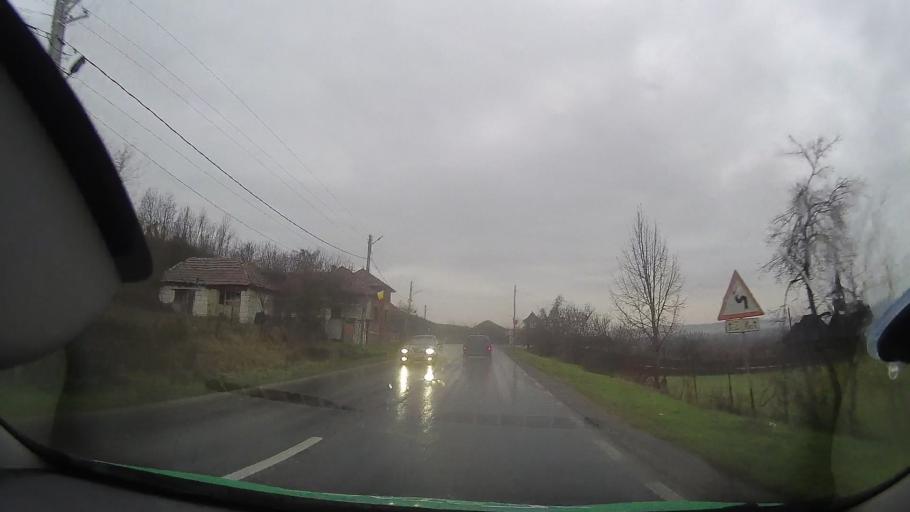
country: RO
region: Bihor
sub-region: Comuna Sambata
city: Sambata
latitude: 46.7619
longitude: 22.1905
